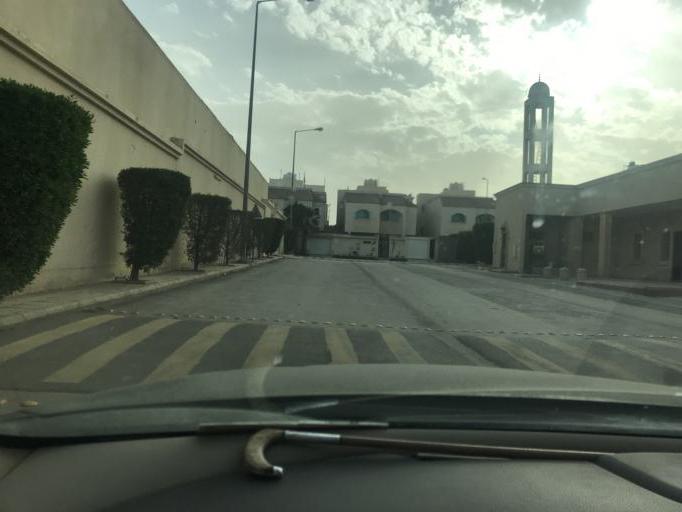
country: SA
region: Ar Riyad
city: Riyadh
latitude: 24.7806
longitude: 46.7137
